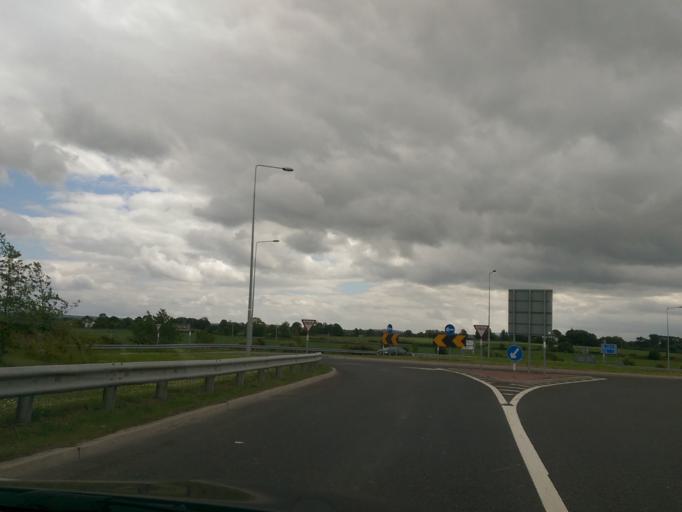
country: IE
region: Munster
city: Thurles
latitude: 52.6229
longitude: -7.7740
